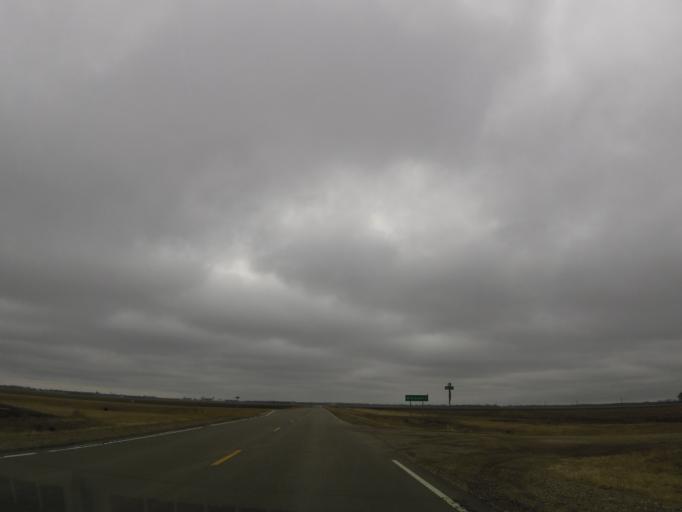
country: US
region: North Dakota
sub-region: Cass County
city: Horace
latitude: 46.6299
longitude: -97.0751
